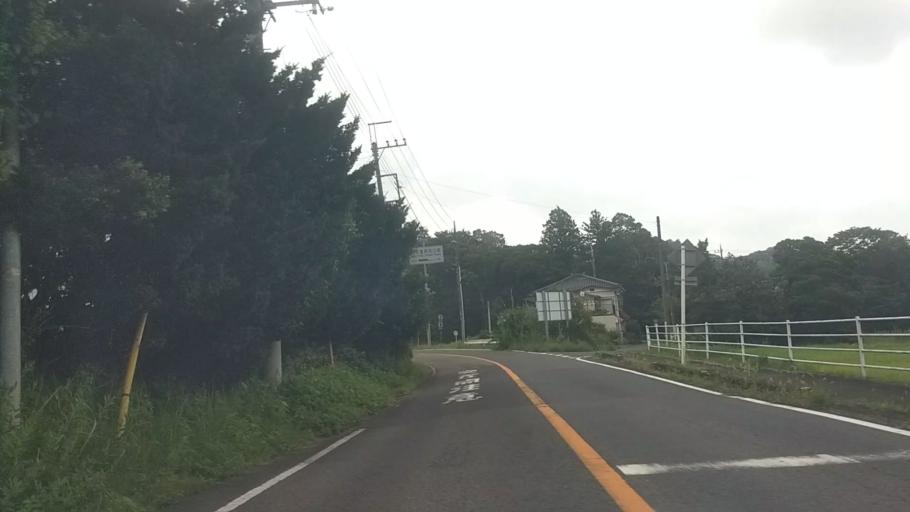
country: JP
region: Chiba
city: Katsuura
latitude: 35.2511
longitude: 140.1958
